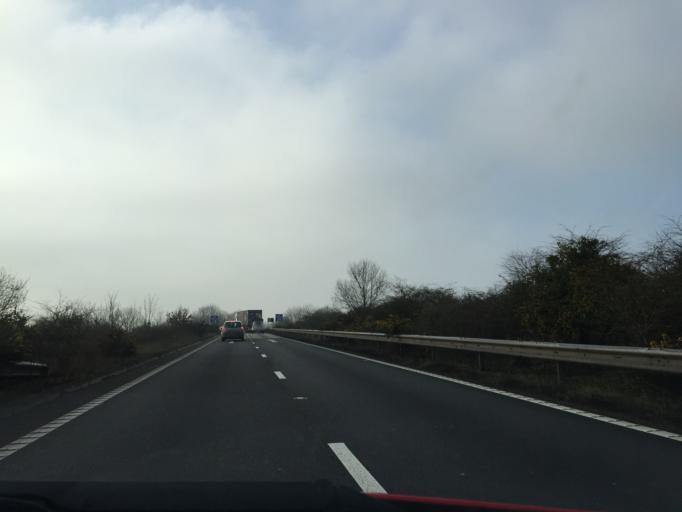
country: GB
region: England
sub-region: Hampshire
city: Totton
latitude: 50.9355
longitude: -1.4729
